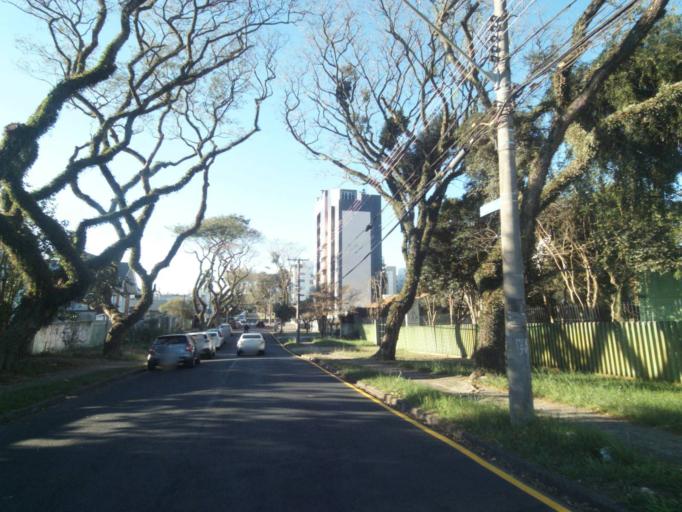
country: BR
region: Parana
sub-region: Curitiba
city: Curitiba
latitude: -25.4617
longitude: -49.2981
